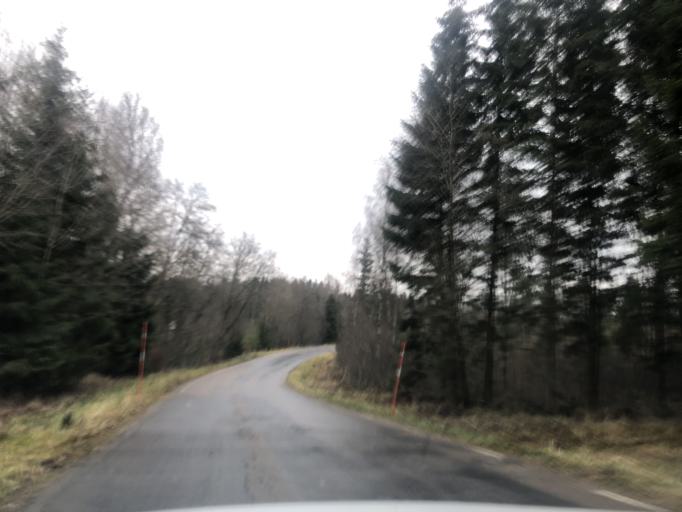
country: SE
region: Vaestra Goetaland
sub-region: Ulricehamns Kommun
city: Ulricehamn
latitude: 57.8777
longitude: 13.5230
